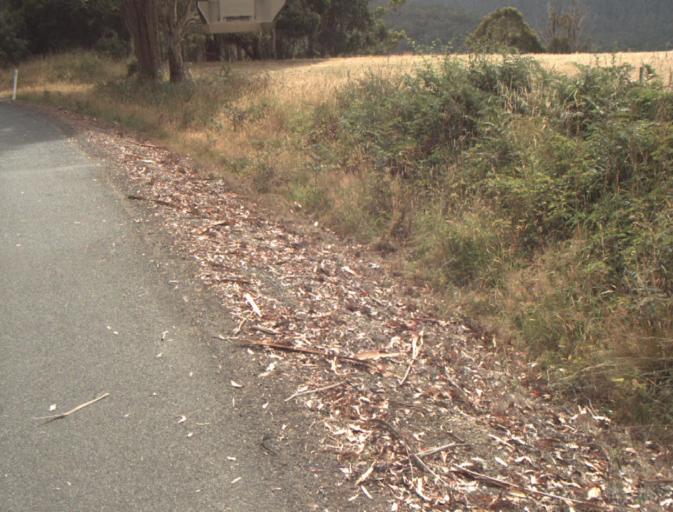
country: AU
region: Tasmania
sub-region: Dorset
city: Scottsdale
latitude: -41.4558
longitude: 147.5979
